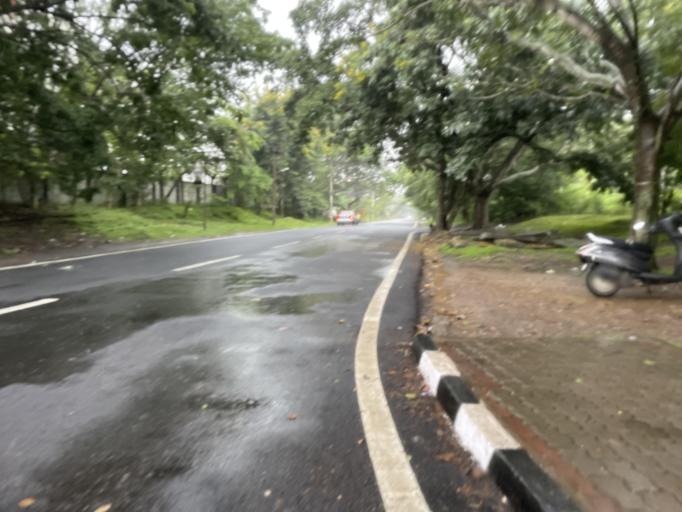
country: IN
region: Karnataka
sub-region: Bangalore Urban
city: Bangalore
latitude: 12.9420
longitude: 77.5057
